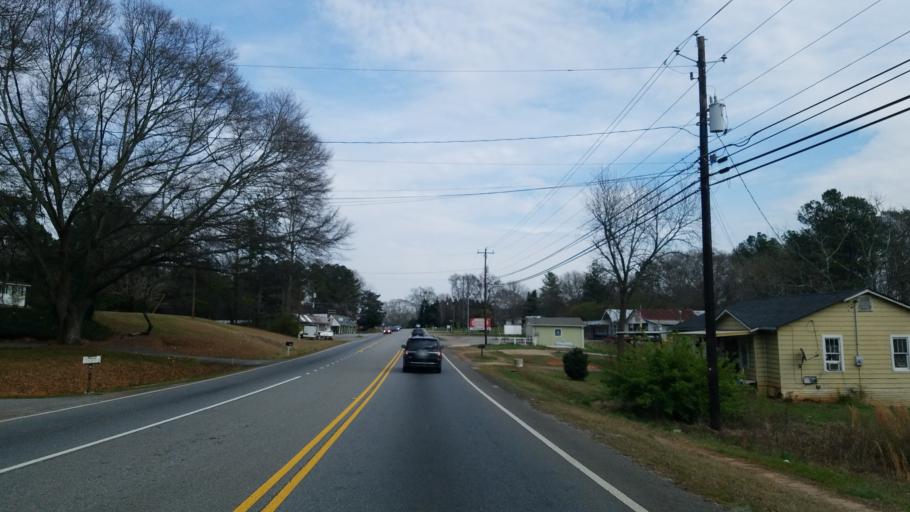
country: US
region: Georgia
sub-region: Cherokee County
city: Ball Ground
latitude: 34.2542
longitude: -84.3534
